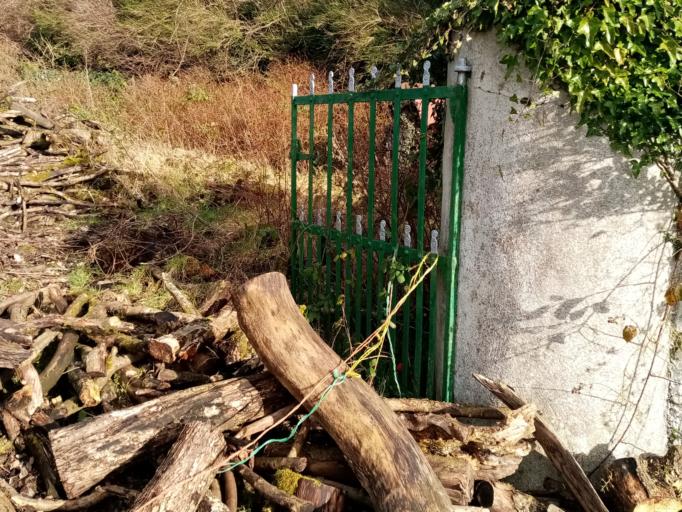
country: IE
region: Munster
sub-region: North Tipperary
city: Templemore
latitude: 52.7555
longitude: -8.0027
